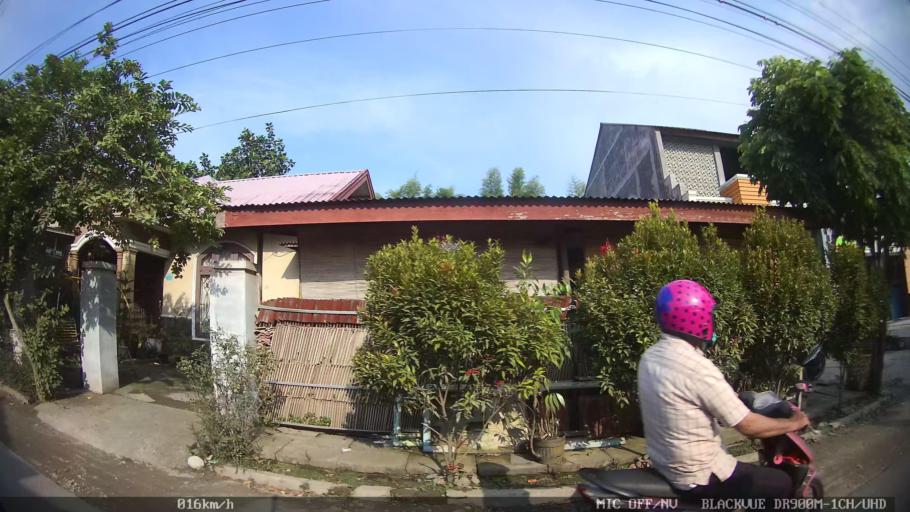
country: ID
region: North Sumatra
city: Medan
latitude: 3.6012
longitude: 98.7417
